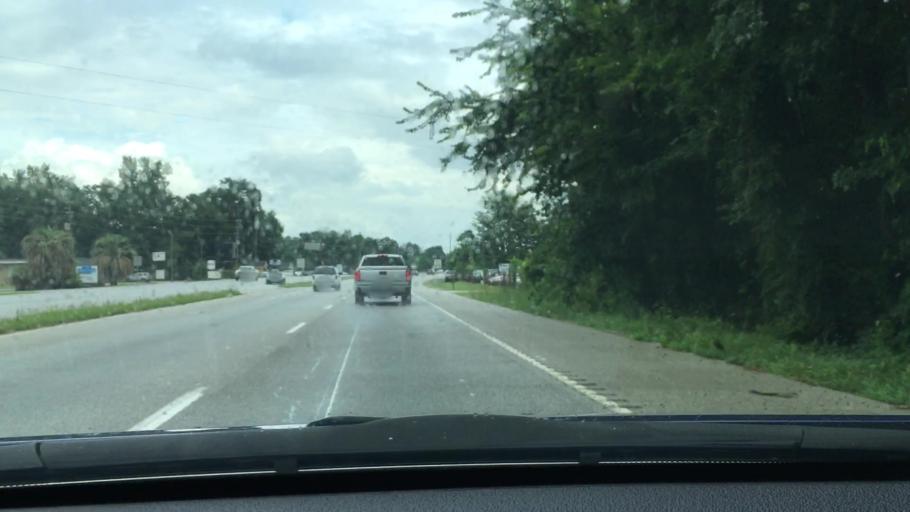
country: US
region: South Carolina
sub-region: Sumter County
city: Cherryvale
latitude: 33.9632
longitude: -80.4200
